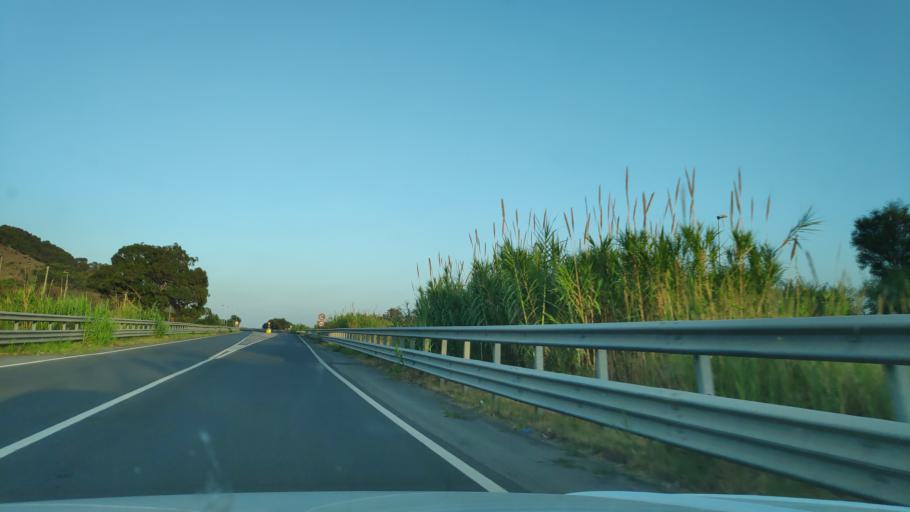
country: IT
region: Calabria
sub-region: Provincia di Reggio Calabria
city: Palizzi Marina
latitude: 37.9223
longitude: 15.9565
